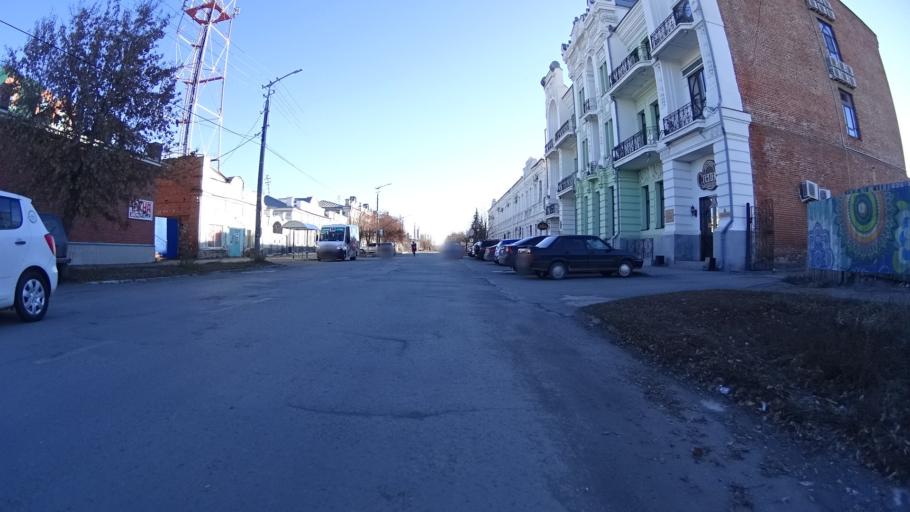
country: RU
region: Chelyabinsk
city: Troitsk
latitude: 54.0843
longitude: 61.5590
